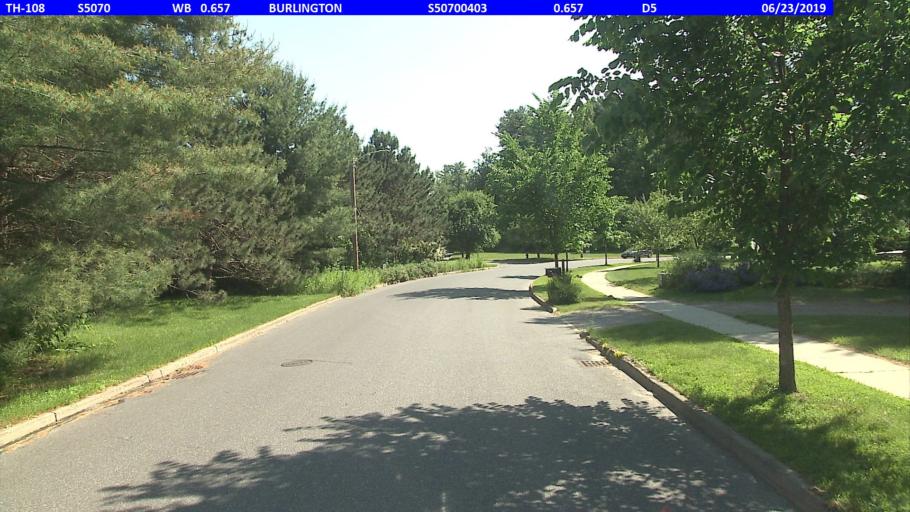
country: US
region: Vermont
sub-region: Chittenden County
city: Burlington
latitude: 44.5067
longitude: -73.2610
